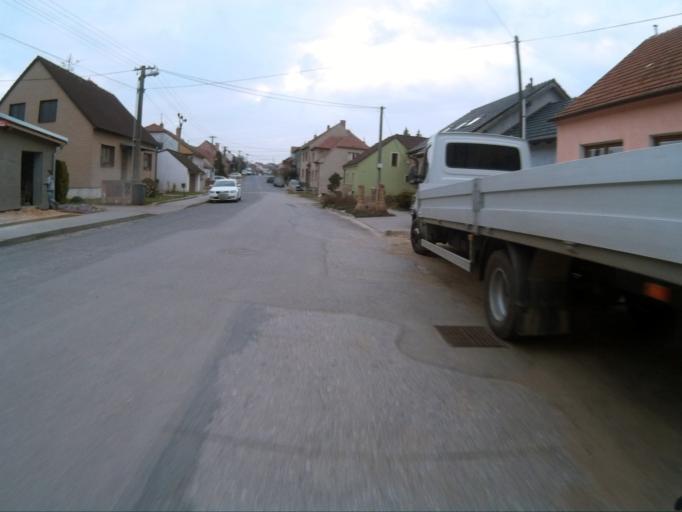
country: CZ
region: South Moravian
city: Nosislav
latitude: 49.0098
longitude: 16.6677
